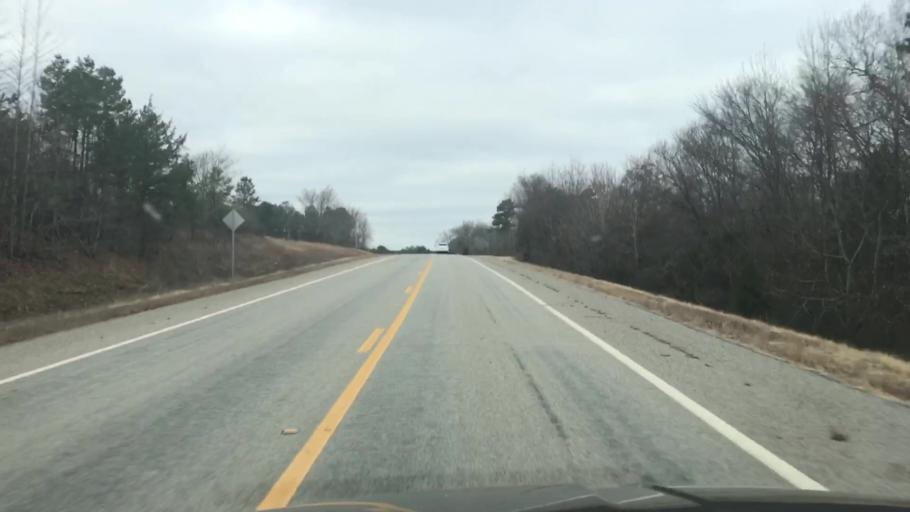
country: US
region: Arkansas
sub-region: Scott County
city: Waldron
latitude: 34.7021
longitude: -93.9184
